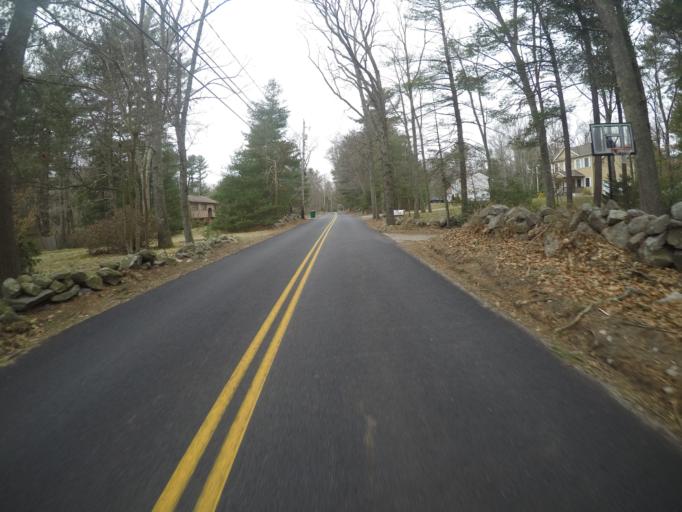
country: US
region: Massachusetts
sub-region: Bristol County
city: Easton
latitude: 42.0344
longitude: -71.1556
